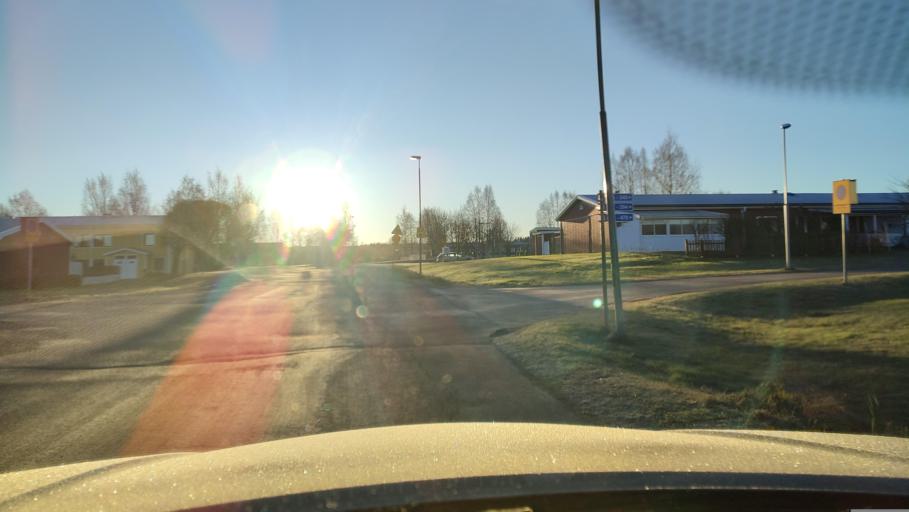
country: SE
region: Vaesterbotten
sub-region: Skelleftea Kommun
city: Skelleftea
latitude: 64.7427
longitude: 20.9836
